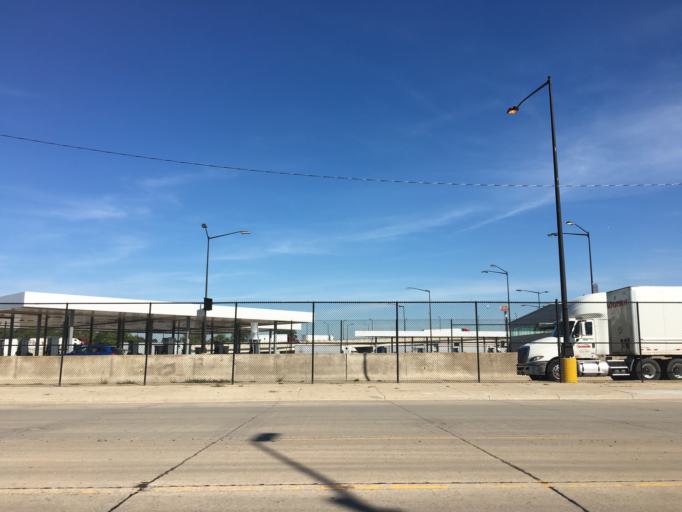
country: US
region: Michigan
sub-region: Wayne County
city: Detroit
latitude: 42.3165
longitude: -83.0803
